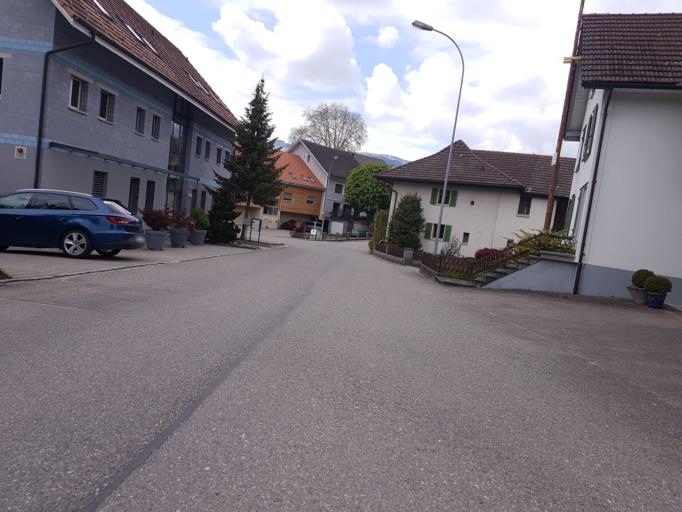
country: CH
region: Bern
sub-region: Seeland District
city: Leuzigen
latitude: 47.1741
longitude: 7.4580
